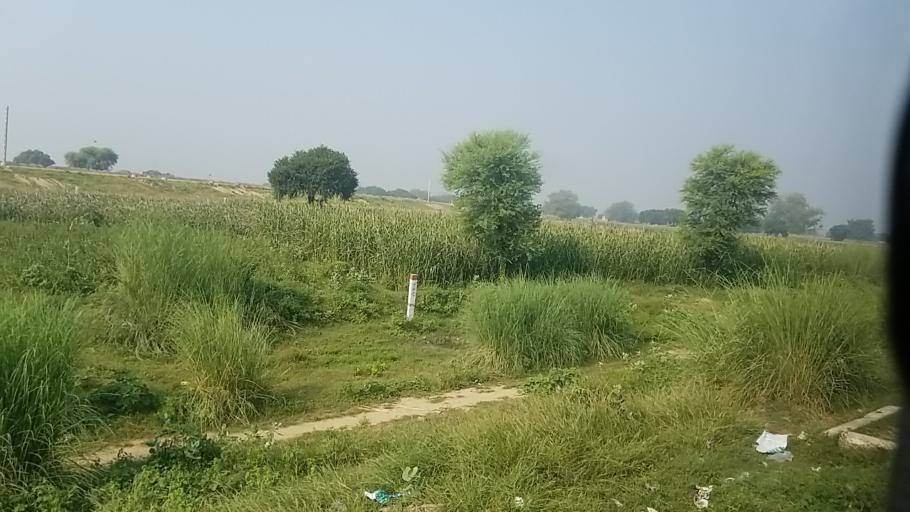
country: IN
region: Uttar Pradesh
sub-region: Firozabad
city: Tundla
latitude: 27.1968
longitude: 78.2614
